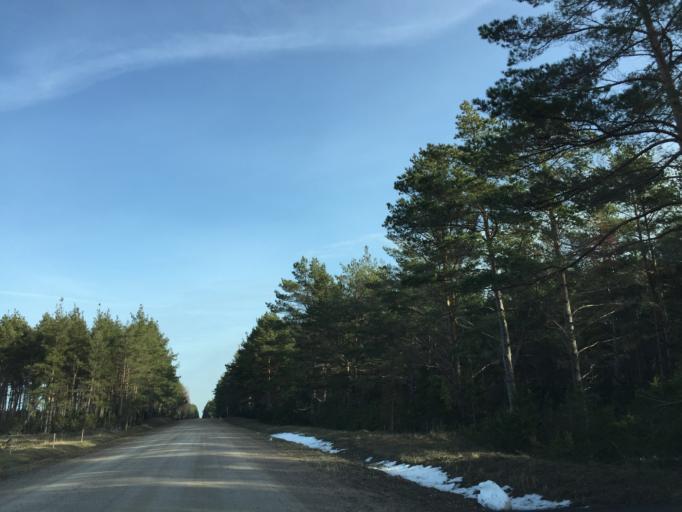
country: EE
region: Saare
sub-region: Kuressaare linn
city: Kuressaare
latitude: 58.2831
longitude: 21.9221
